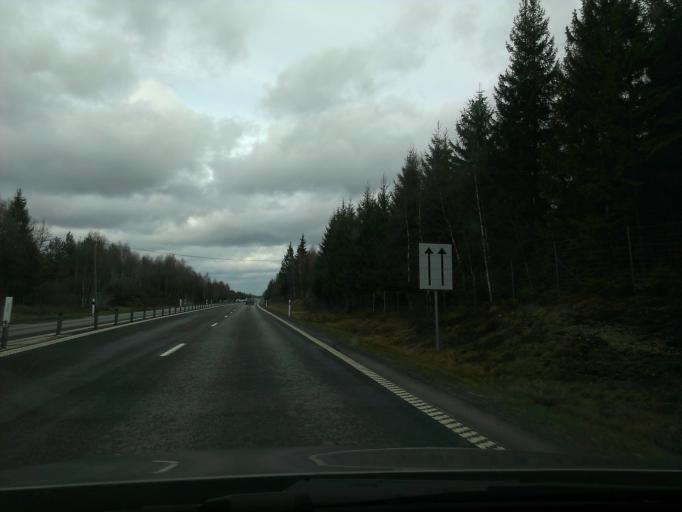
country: SE
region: Kronoberg
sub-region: Almhults Kommun
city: AElmhult
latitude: 56.4766
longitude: 14.1086
